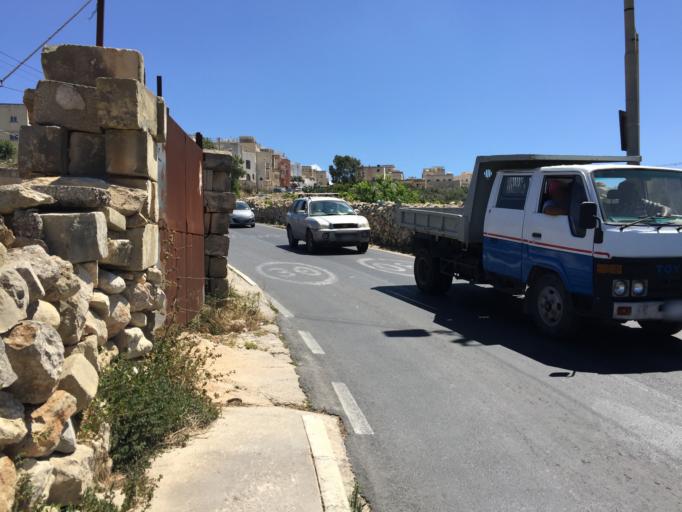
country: MT
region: Is-Swieqi
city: Swieqi
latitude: 35.9157
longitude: 14.4789
